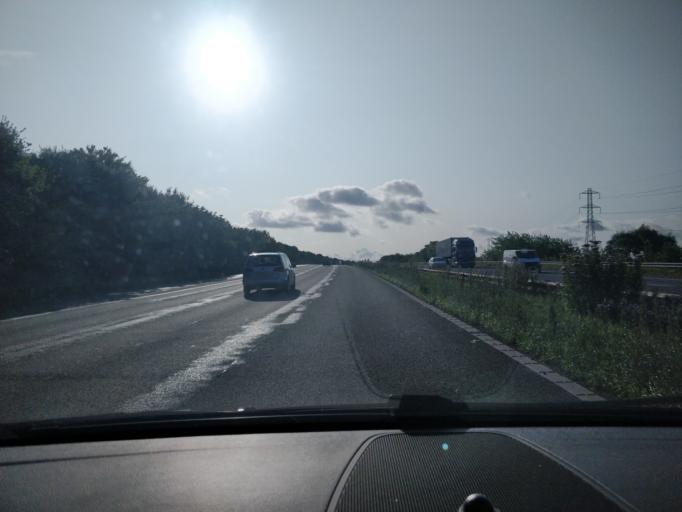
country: GB
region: England
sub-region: Sefton
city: Melling
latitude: 53.4850
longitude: -2.9254
